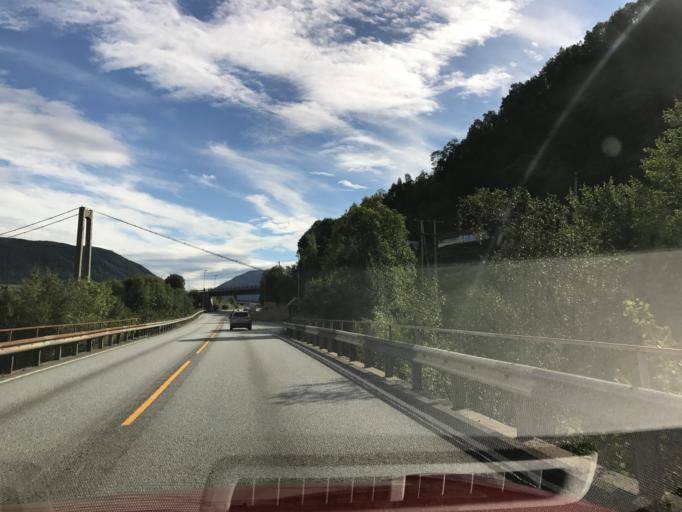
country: NO
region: Hordaland
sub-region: Bergen
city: Indre Arna
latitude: 60.4207
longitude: 5.5310
